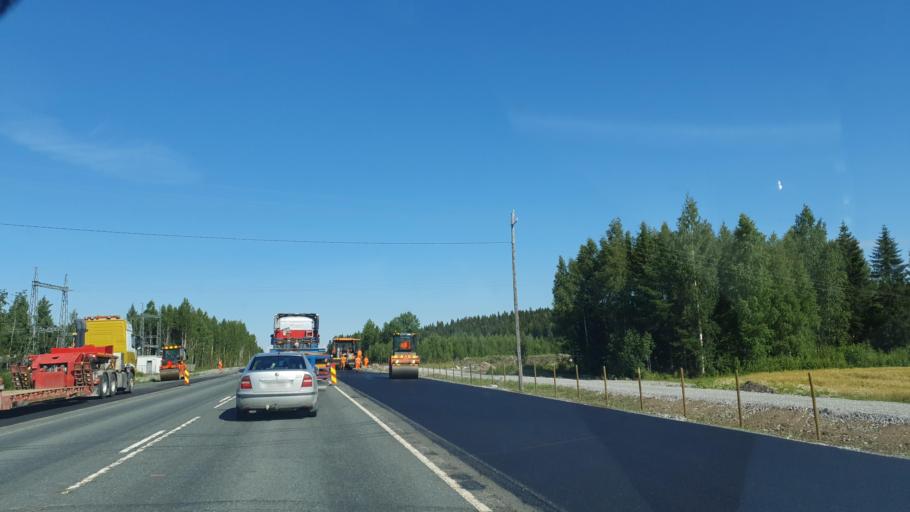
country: FI
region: Northern Savo
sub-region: Ylae-Savo
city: Lapinlahti
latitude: 63.2889
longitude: 27.4546
